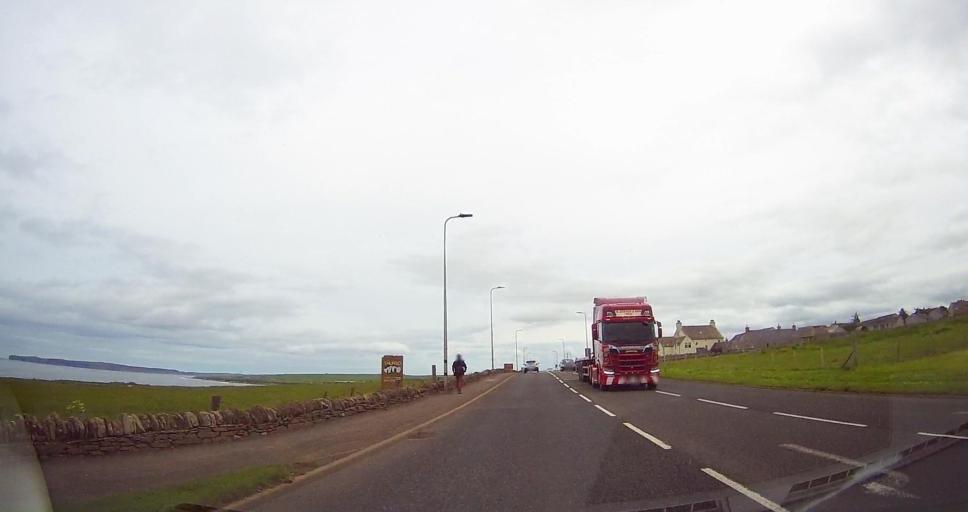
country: GB
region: Scotland
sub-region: Highland
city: Thurso
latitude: 58.5985
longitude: -3.5366
